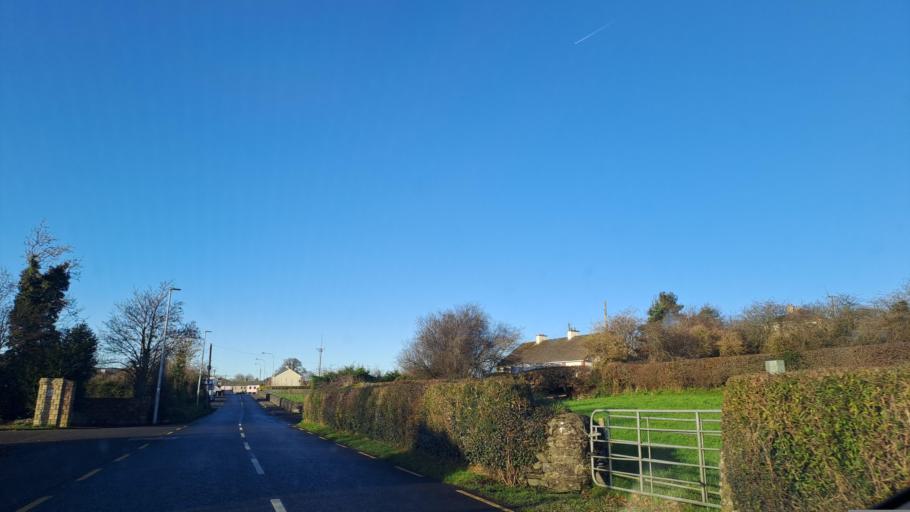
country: IE
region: Ulster
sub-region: An Cabhan
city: Mullagh
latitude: 53.8097
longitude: -6.9404
